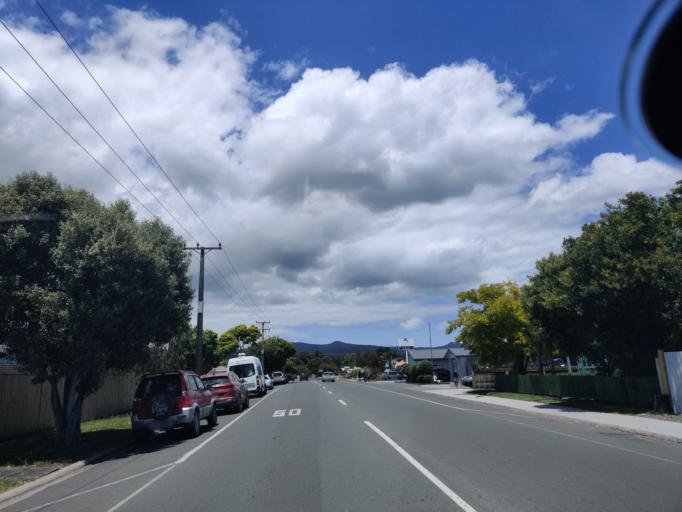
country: NZ
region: Northland
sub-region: Far North District
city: Kaitaia
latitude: -35.1094
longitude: 173.2587
